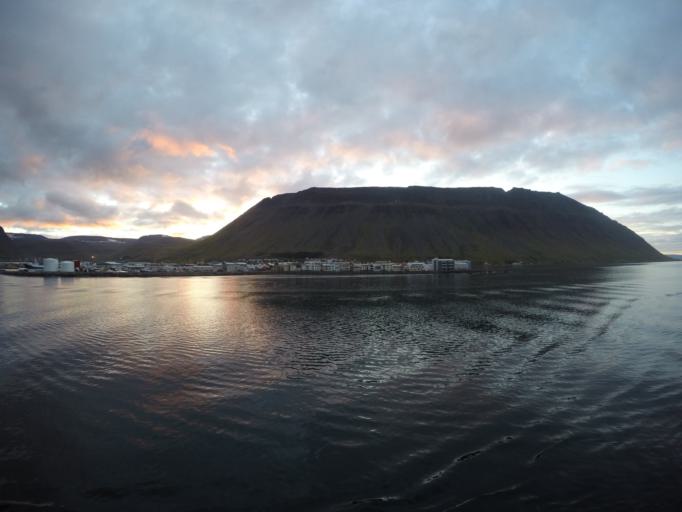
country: IS
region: Westfjords
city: Isafjoerdur
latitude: 66.0692
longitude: -23.1092
